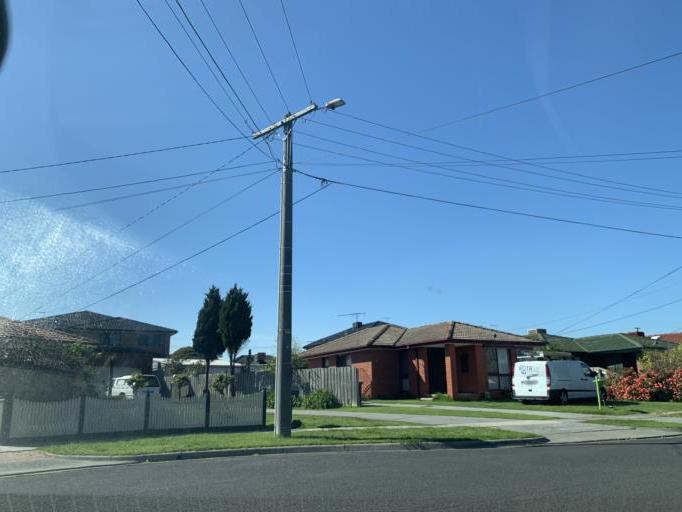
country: AU
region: Victoria
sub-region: Greater Dandenong
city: Dandenong
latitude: -38.0007
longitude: 145.2046
